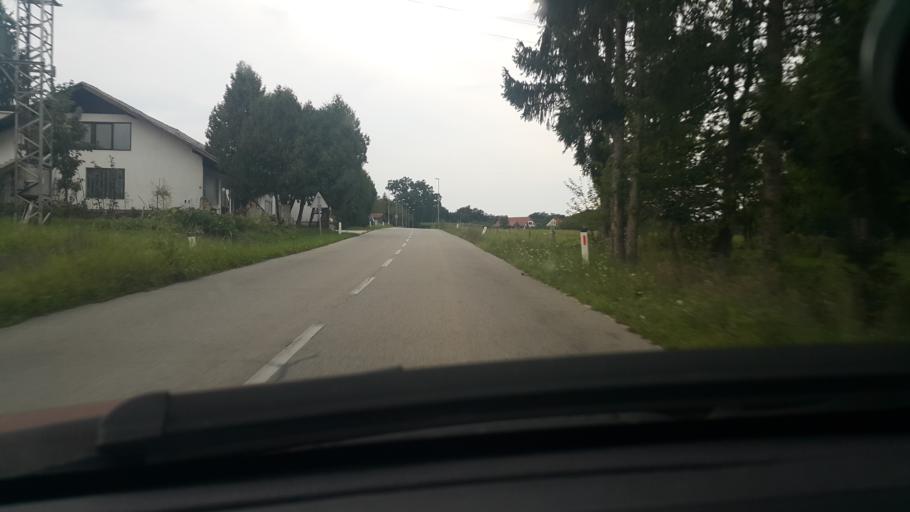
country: SI
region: Brezice
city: Brezice
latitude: 45.9212
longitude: 15.6682
